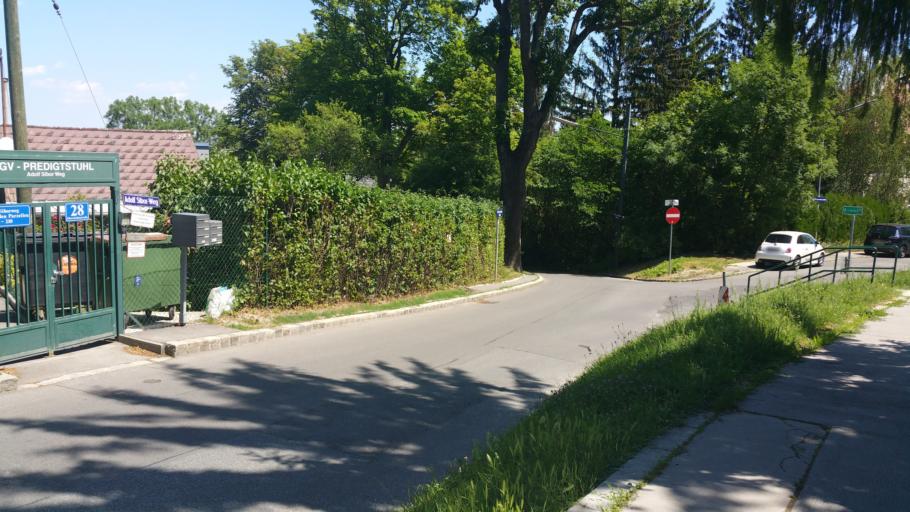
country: AT
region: Vienna
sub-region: Wien Stadt
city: Vienna
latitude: 48.2246
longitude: 16.2970
